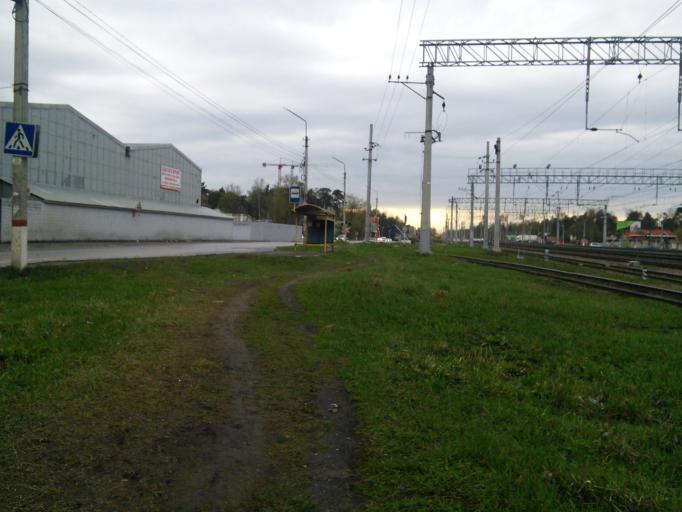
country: RU
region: Moskovskaya
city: Bykovo
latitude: 55.6294
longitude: 38.0611
